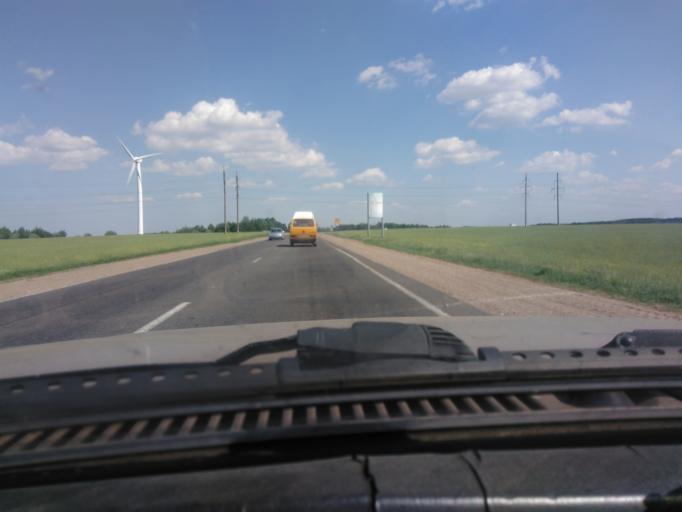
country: BY
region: Mogilev
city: Palykavichy Pyershyya
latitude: 53.9793
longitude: 30.3424
